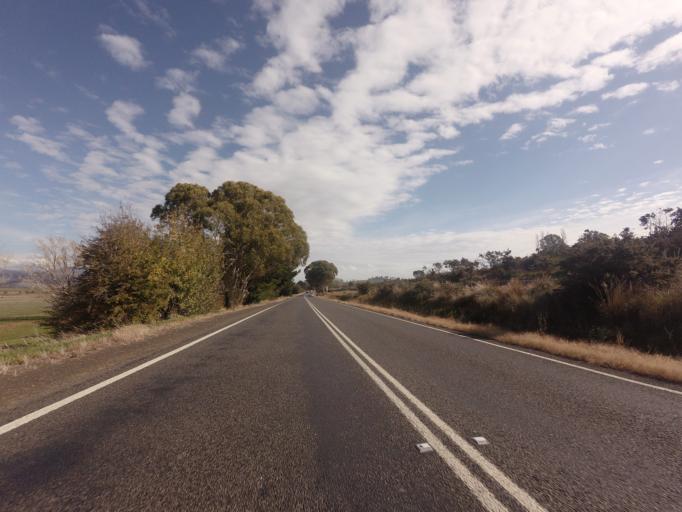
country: AU
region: Tasmania
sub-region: Meander Valley
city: Westbury
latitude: -41.5267
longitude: 146.8152
